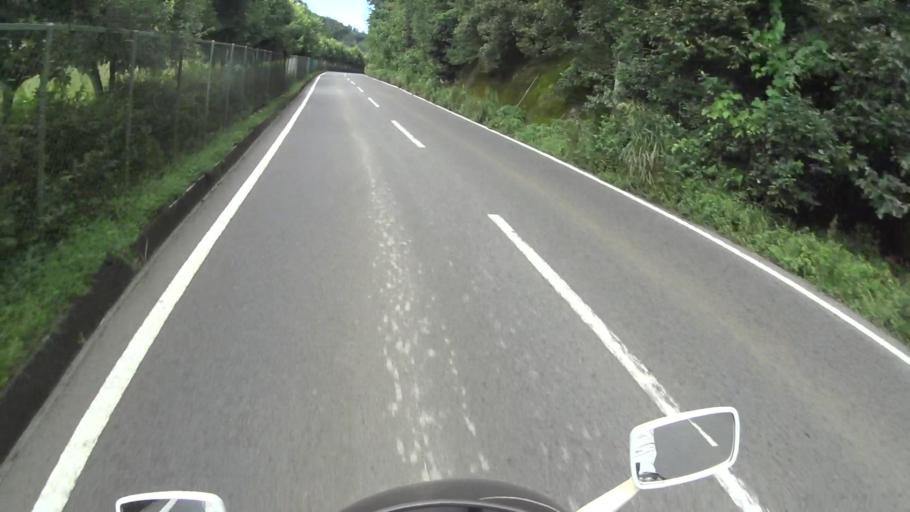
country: JP
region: Shiga Prefecture
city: Otsu-shi
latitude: 34.9242
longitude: 135.8860
